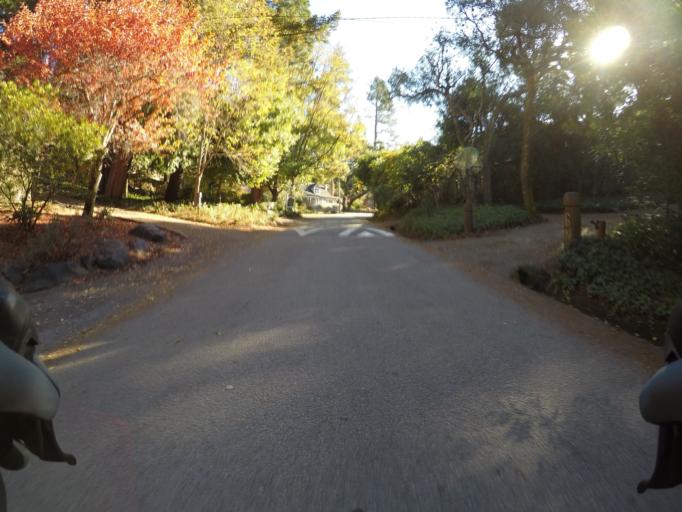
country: US
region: California
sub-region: Santa Cruz County
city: Mount Hermon
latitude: 37.0517
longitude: -122.0544
